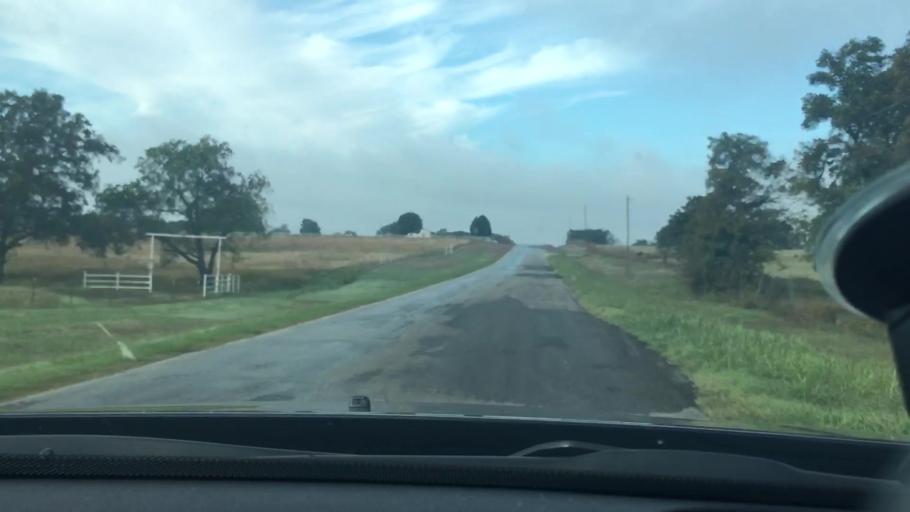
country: US
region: Oklahoma
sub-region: Murray County
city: Sulphur
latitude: 34.6223
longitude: -96.9533
